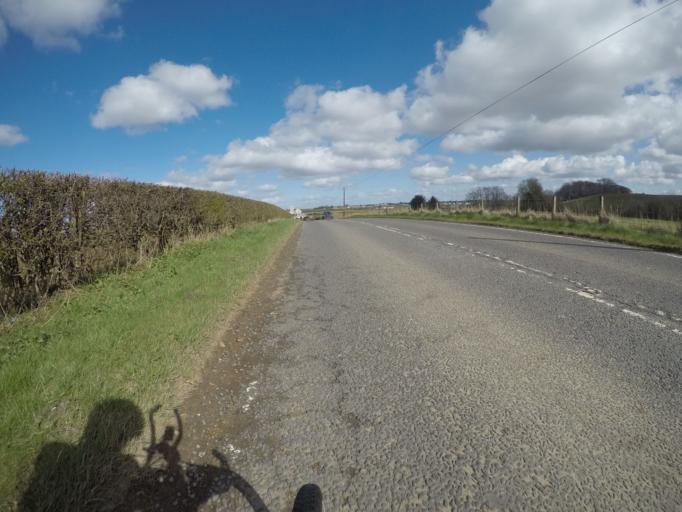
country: GB
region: Scotland
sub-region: East Ayrshire
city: Crosshouse
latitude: 55.5900
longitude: -4.5543
